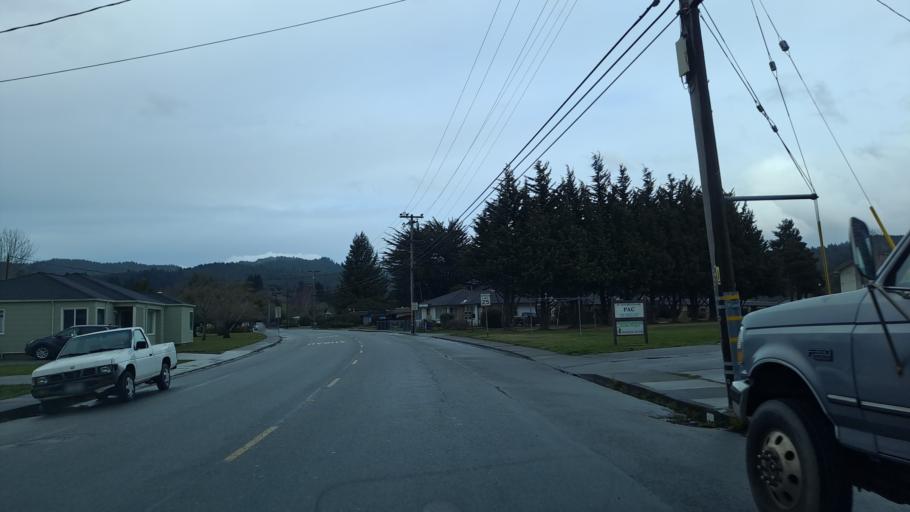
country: US
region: California
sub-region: Humboldt County
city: Fortuna
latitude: 40.5893
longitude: -124.1423
